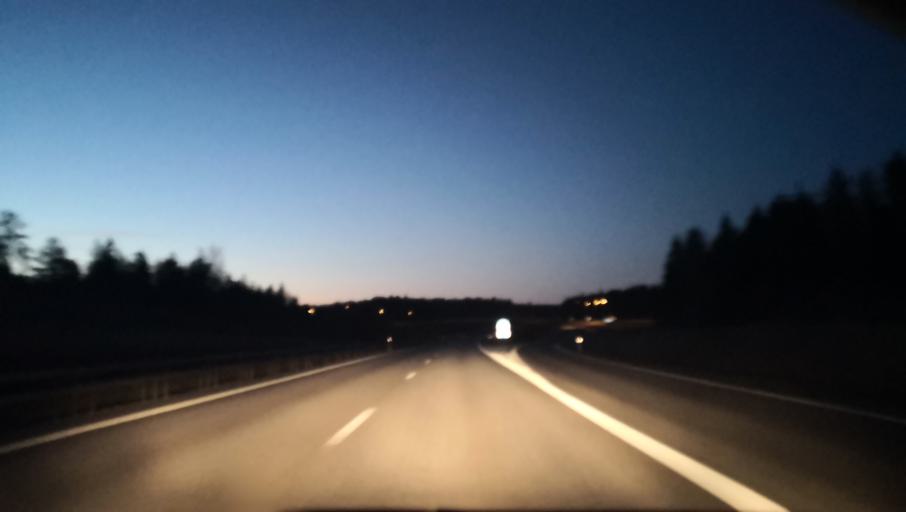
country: SE
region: Stockholm
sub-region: Nynashamns Kommun
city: Osmo
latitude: 59.0229
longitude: 17.9497
